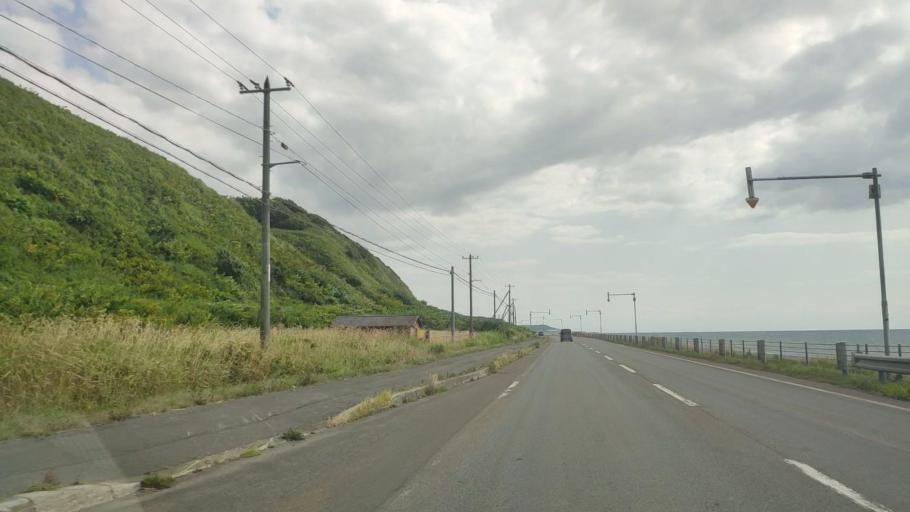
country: JP
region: Hokkaido
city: Rumoi
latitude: 44.1982
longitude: 141.6579
